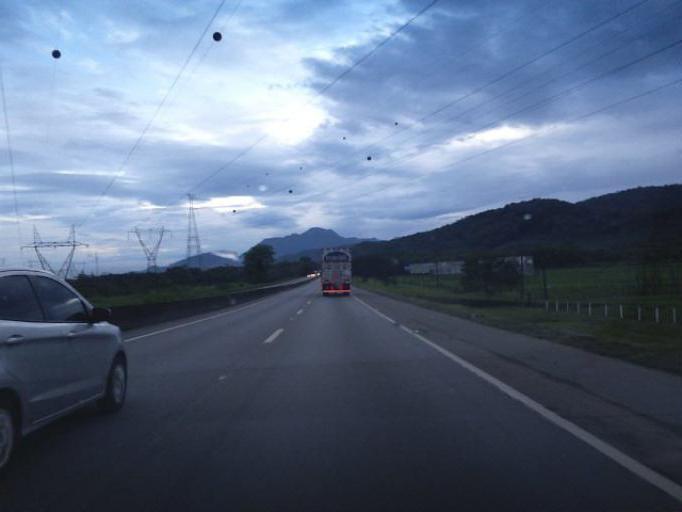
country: BR
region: Santa Catarina
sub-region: Joinville
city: Joinville
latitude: -26.1171
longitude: -48.8788
